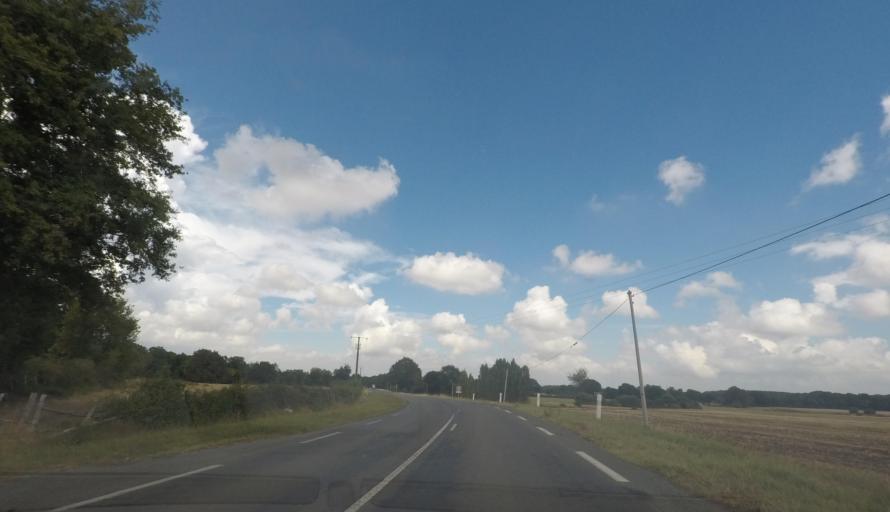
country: FR
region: Pays de la Loire
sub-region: Departement de la Sarthe
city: Bonnetable
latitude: 48.2110
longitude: 0.4333
